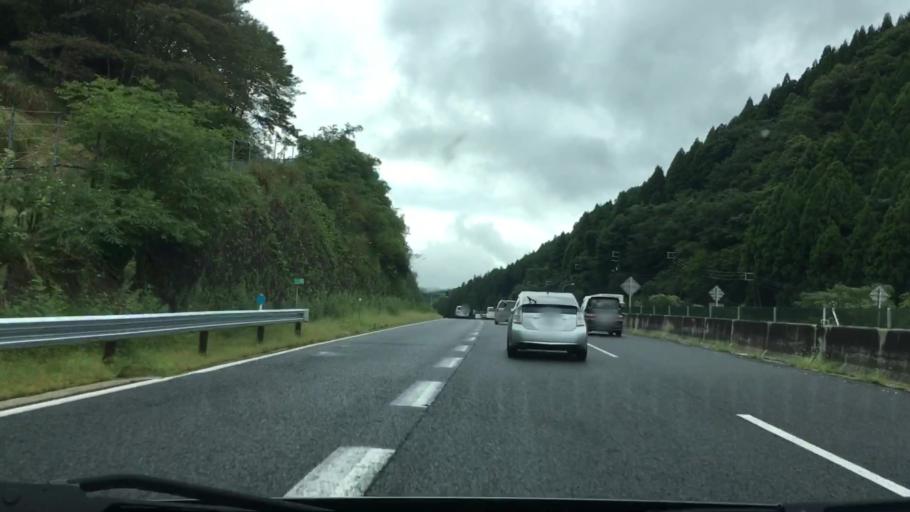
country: JP
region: Hyogo
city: Yamazakicho-nakabirose
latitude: 35.0411
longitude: 134.4689
